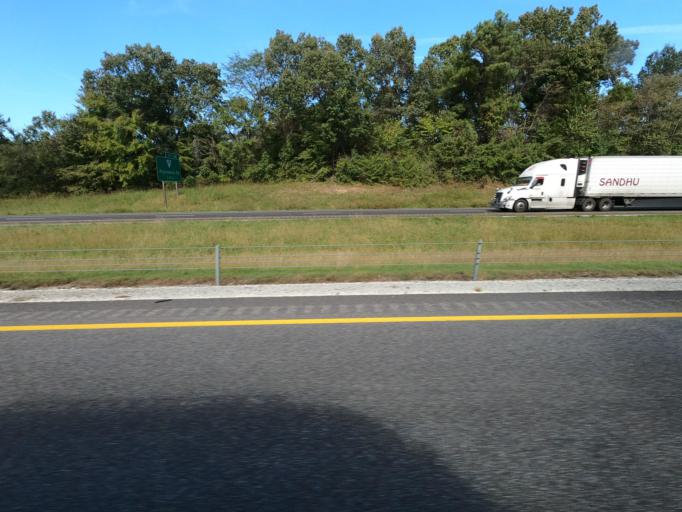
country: US
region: Tennessee
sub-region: Crockett County
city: Bells
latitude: 35.6040
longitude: -89.0367
